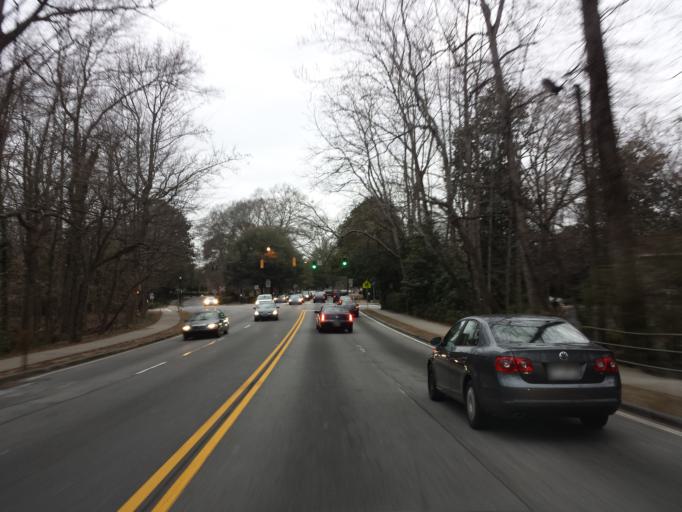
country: US
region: Georgia
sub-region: DeKalb County
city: Druid Hills
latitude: 33.7739
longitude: -84.3362
